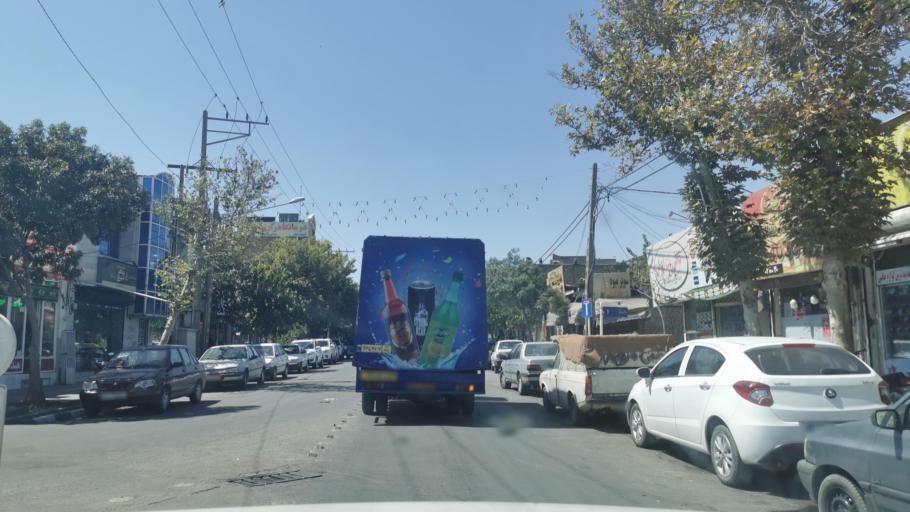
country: IR
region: Razavi Khorasan
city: Mashhad
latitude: 36.3594
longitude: 59.5513
